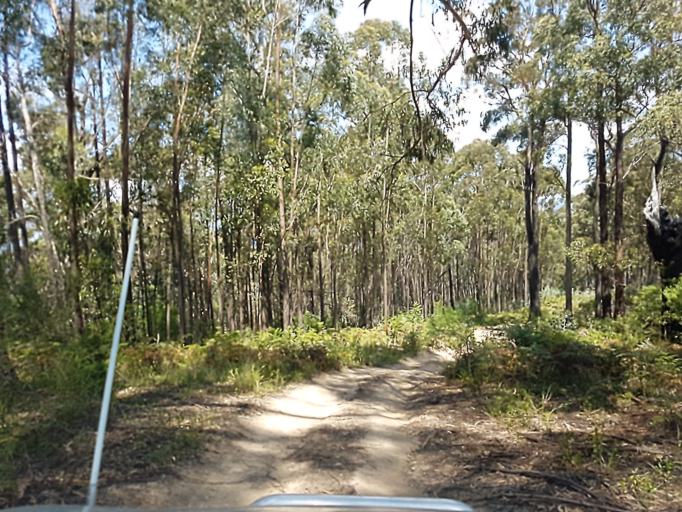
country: AU
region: Victoria
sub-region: East Gippsland
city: Lakes Entrance
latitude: -37.3990
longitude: 148.2982
